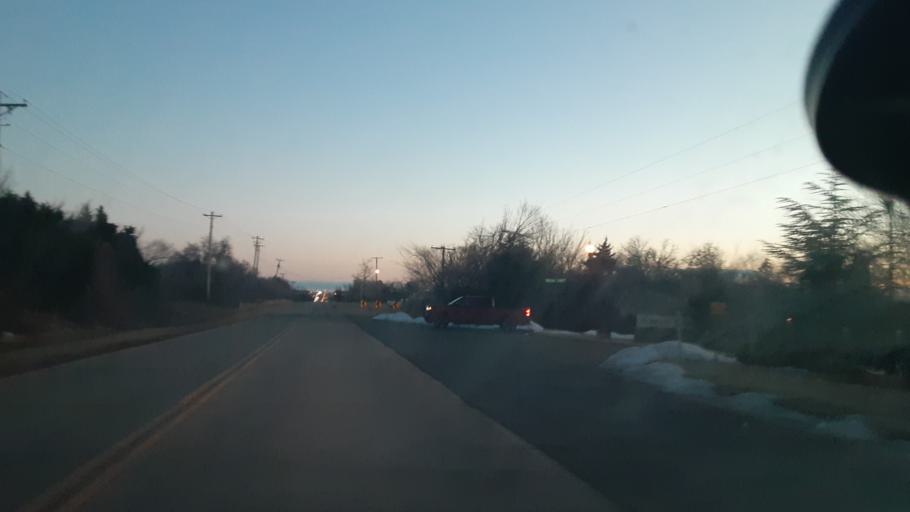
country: US
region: Oklahoma
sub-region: Oklahoma County
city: Edmond
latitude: 35.6601
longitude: -97.4251
